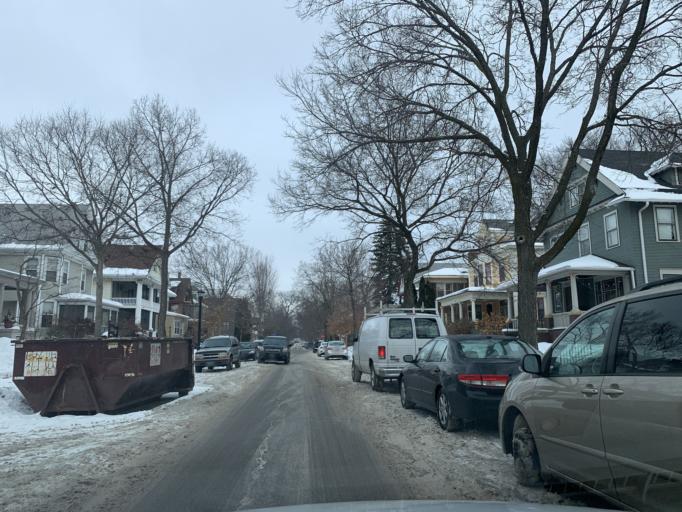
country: US
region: Minnesota
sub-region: Hennepin County
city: Minneapolis
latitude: 44.9581
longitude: -93.2918
